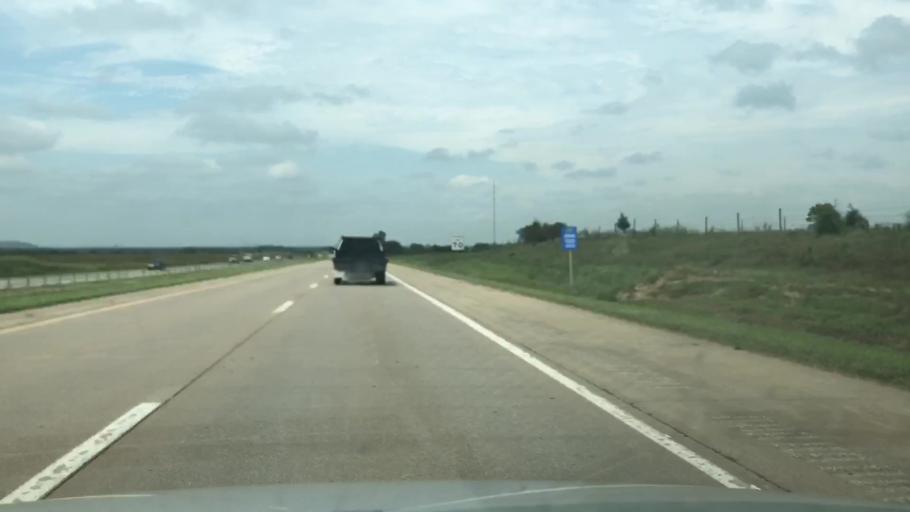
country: US
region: Oklahoma
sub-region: Washington County
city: Bartlesville
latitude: 36.6157
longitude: -95.9354
